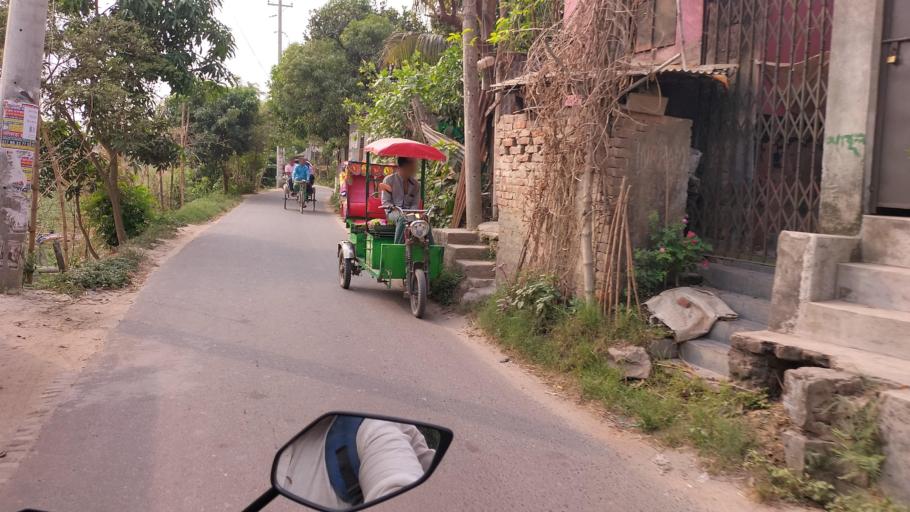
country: BD
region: Dhaka
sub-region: Dhaka
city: Dhaka
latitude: 23.6640
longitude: 90.3535
